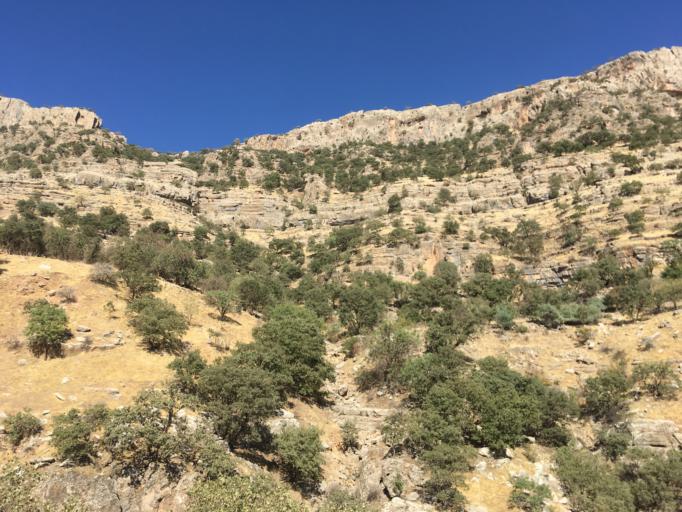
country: IQ
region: Arbil
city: Mergasur
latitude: 36.8359
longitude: 44.2204
